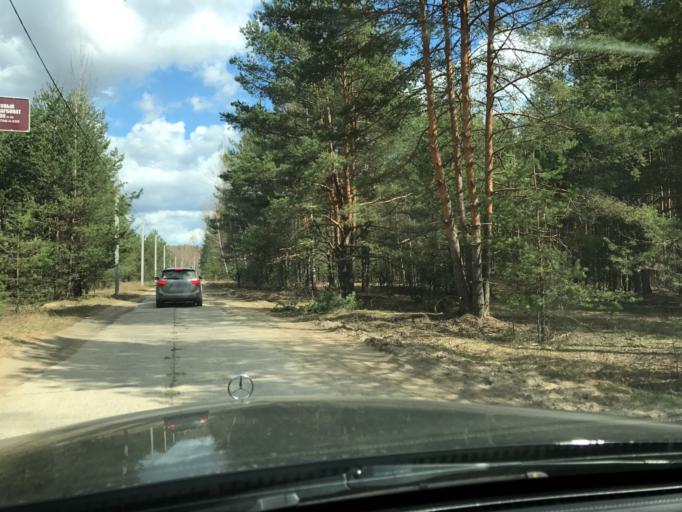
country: RU
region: Vladimir
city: Pokrov
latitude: 55.8583
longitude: 39.2030
